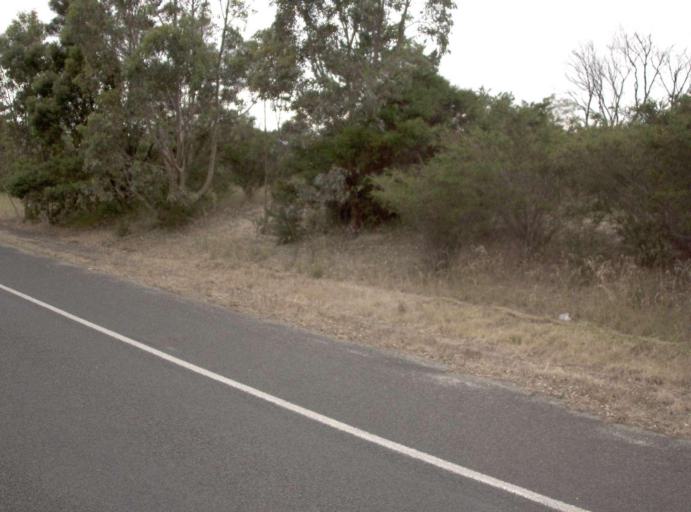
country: AU
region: Victoria
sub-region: Wellington
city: Sale
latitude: -38.1654
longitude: 147.0867
